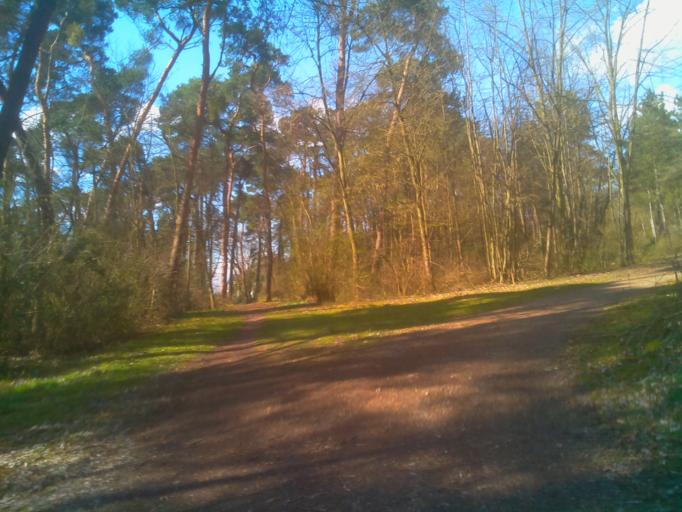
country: DE
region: Baden-Wuerttemberg
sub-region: Karlsruhe Region
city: Ilvesheim
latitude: 49.4441
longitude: 8.5402
